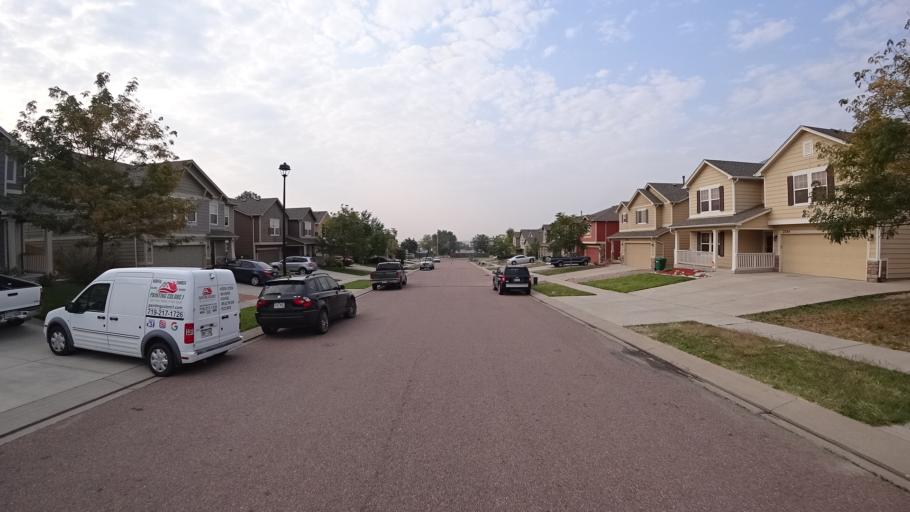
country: US
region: Colorado
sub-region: El Paso County
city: Stratmoor
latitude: 38.7982
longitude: -104.7766
